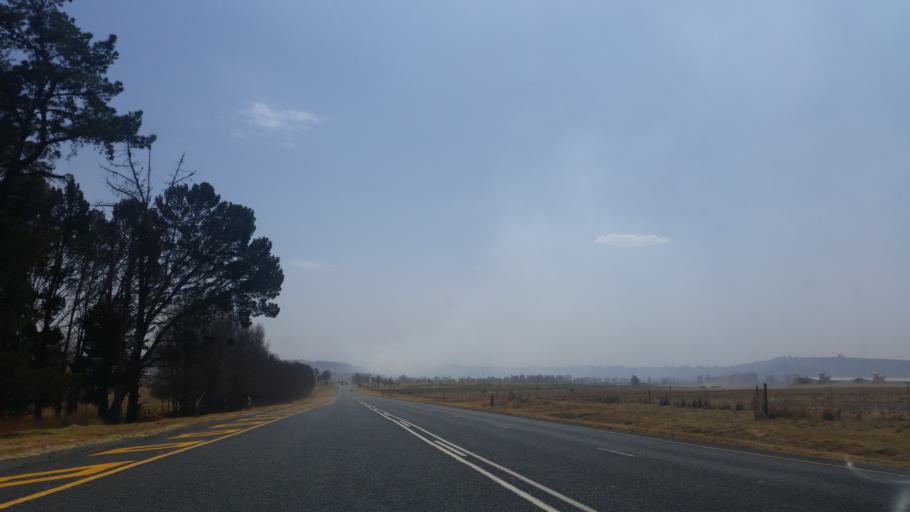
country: ZA
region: Orange Free State
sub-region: Thabo Mofutsanyana District Municipality
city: Bethlehem
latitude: -28.2871
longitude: 28.4037
